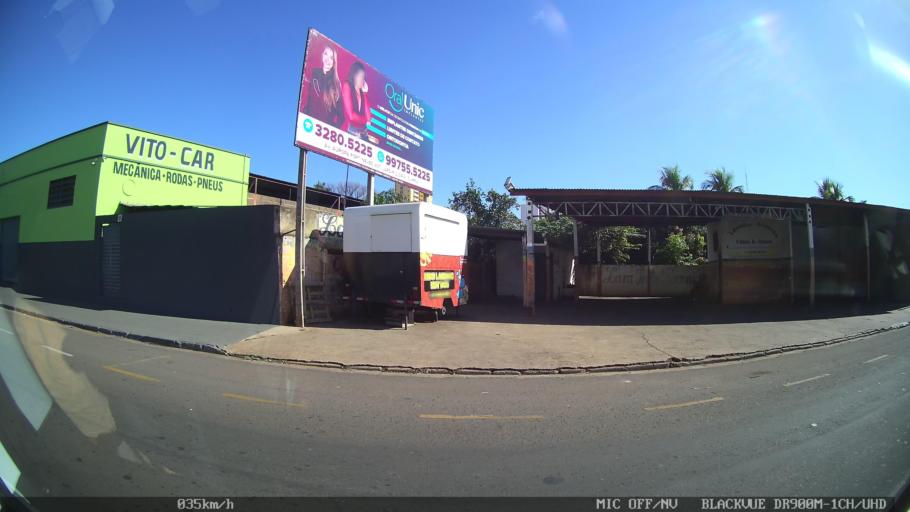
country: BR
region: Sao Paulo
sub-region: Olimpia
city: Olimpia
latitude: -20.7357
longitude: -48.9115
